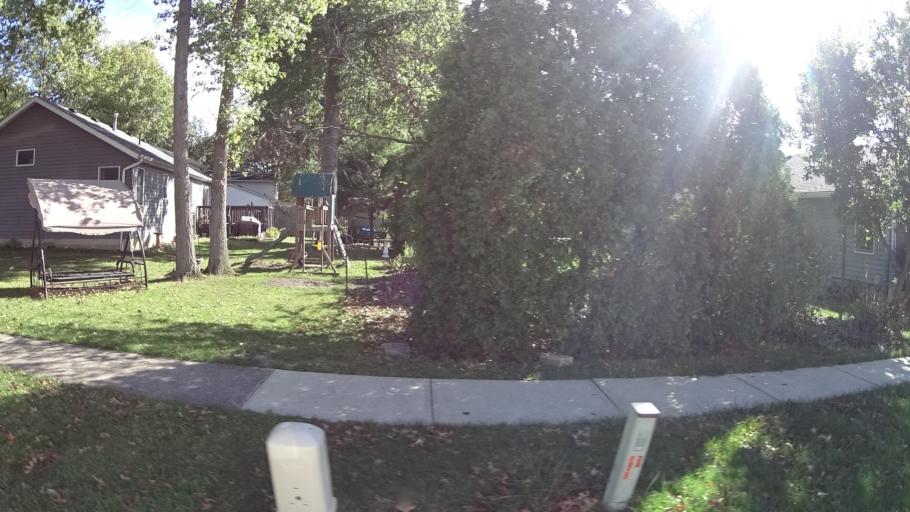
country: US
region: Ohio
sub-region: Lorain County
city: Grafton
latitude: 41.2866
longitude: -82.0609
